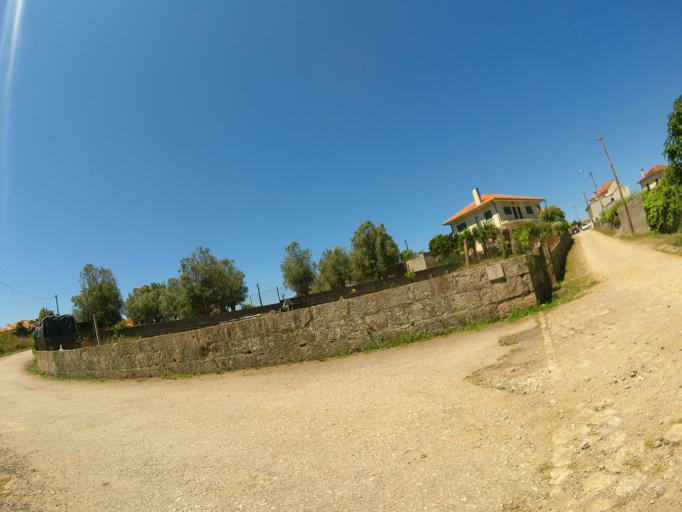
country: PT
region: Viana do Castelo
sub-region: Viana do Castelo
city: Darque
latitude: 41.7152
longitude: -8.7139
